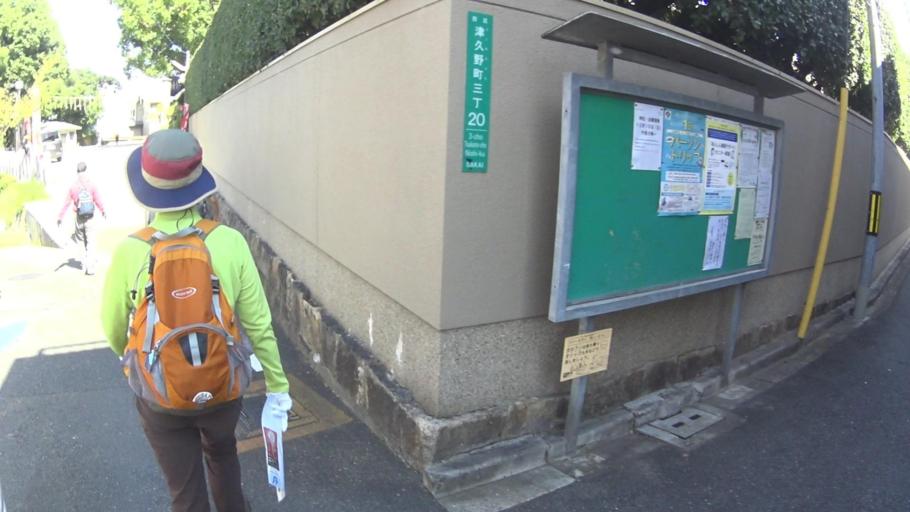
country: JP
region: Osaka
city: Sakai
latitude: 34.5447
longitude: 135.4693
